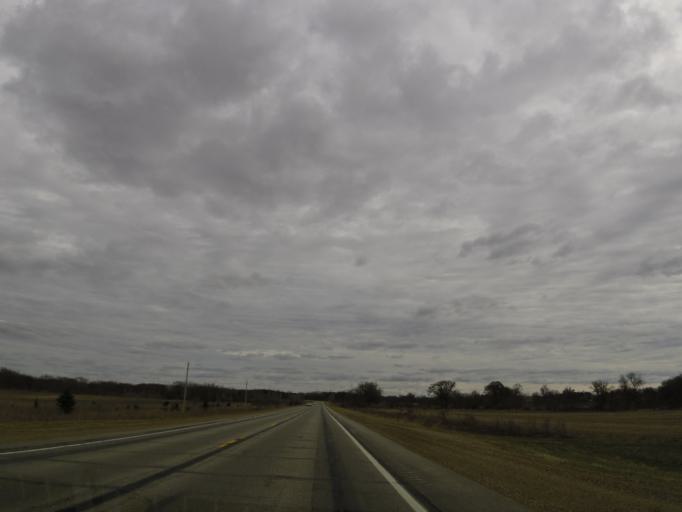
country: US
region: Iowa
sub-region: Howard County
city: Cresco
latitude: 43.4671
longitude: -92.3153
